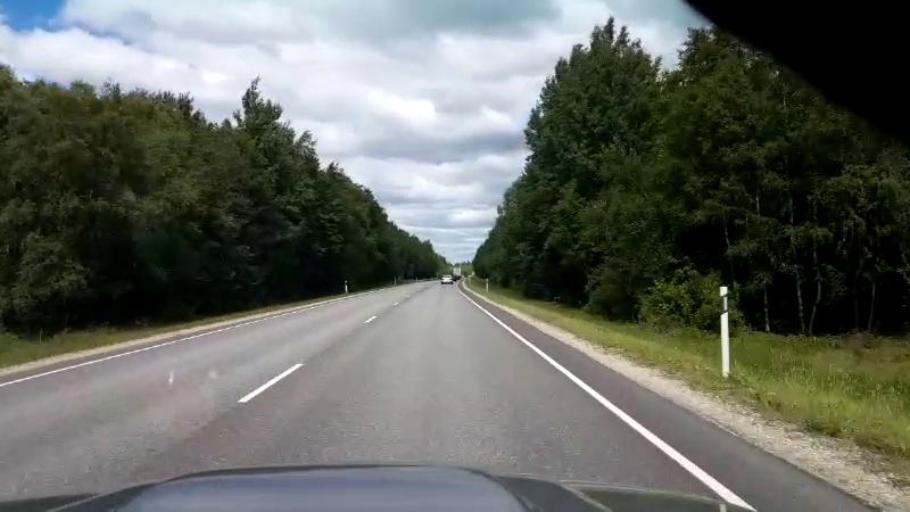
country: EE
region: Paernumaa
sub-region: Halinga vald
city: Parnu-Jaagupi
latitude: 58.6087
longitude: 24.5123
